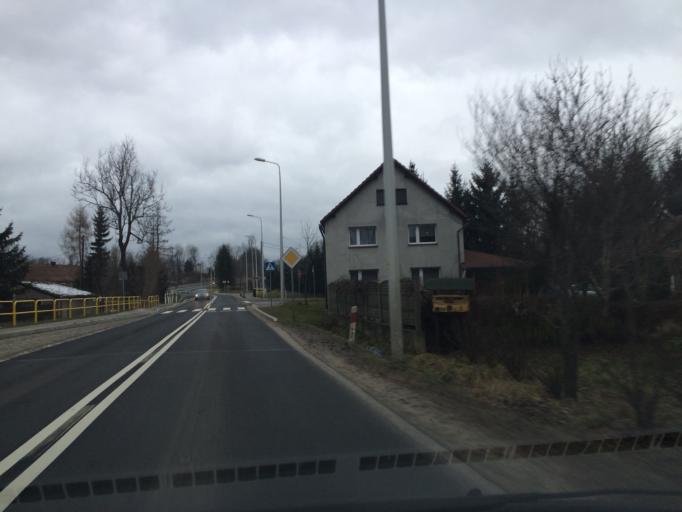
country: PL
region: Lower Silesian Voivodeship
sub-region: Powiat lubanski
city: Pisarzowice
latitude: 51.1663
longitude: 15.2653
